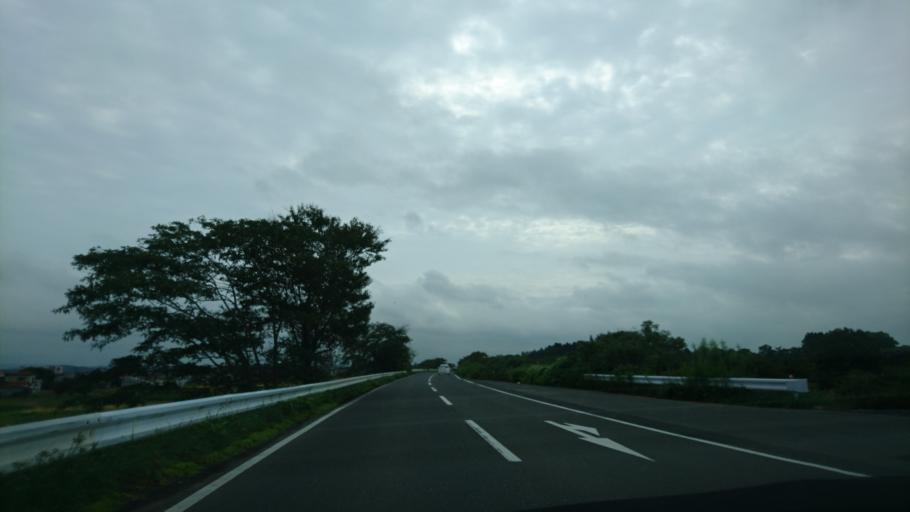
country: JP
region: Iwate
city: Ichinoseki
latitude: 38.7801
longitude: 141.1168
